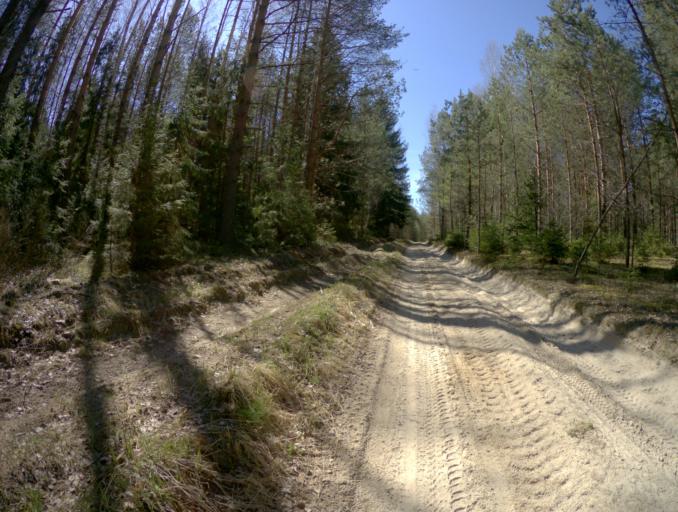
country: RU
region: Vladimir
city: Golovino
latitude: 55.8939
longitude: 40.4163
